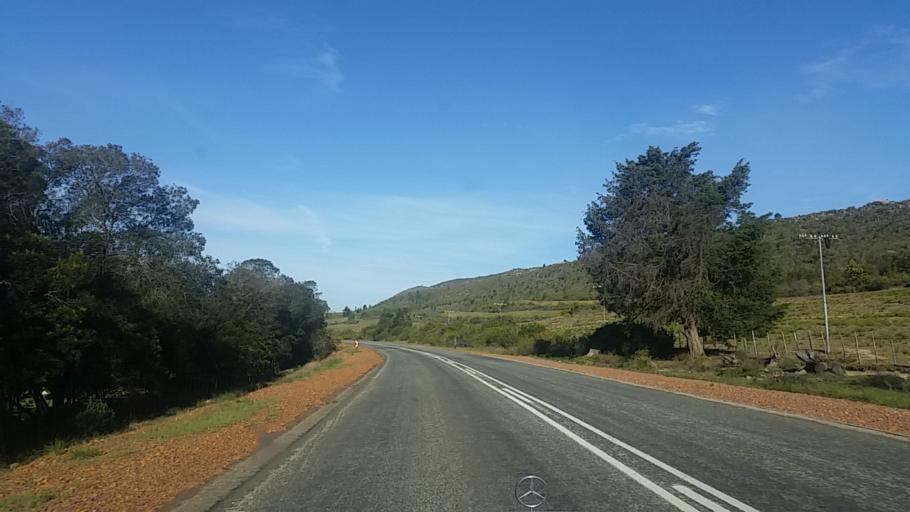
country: ZA
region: Western Cape
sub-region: Eden District Municipality
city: Knysna
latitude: -33.7748
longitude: 22.9061
